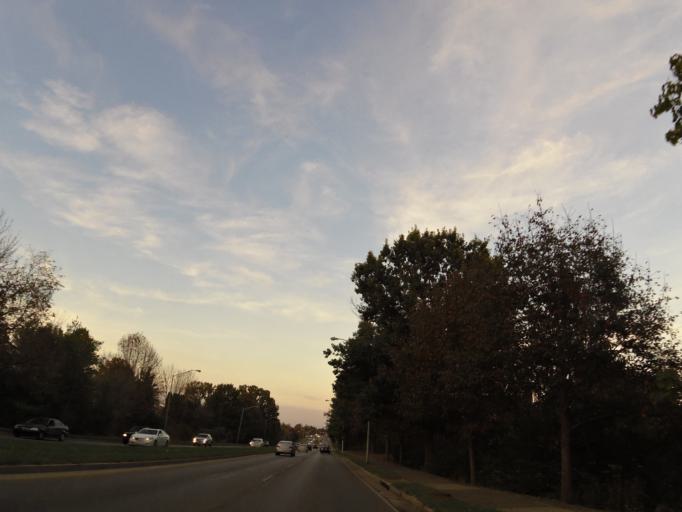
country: US
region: Kentucky
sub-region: Fayette County
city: Lexington
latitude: 37.9797
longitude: -84.4626
